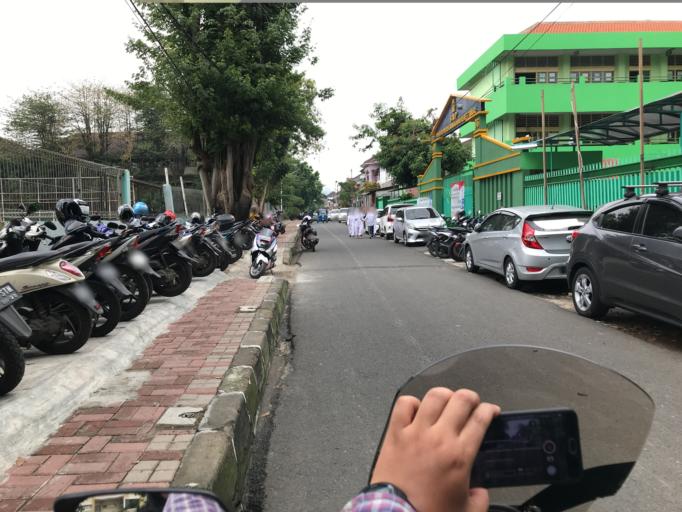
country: ID
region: Jakarta Raya
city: Jakarta
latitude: -6.2356
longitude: 106.8567
